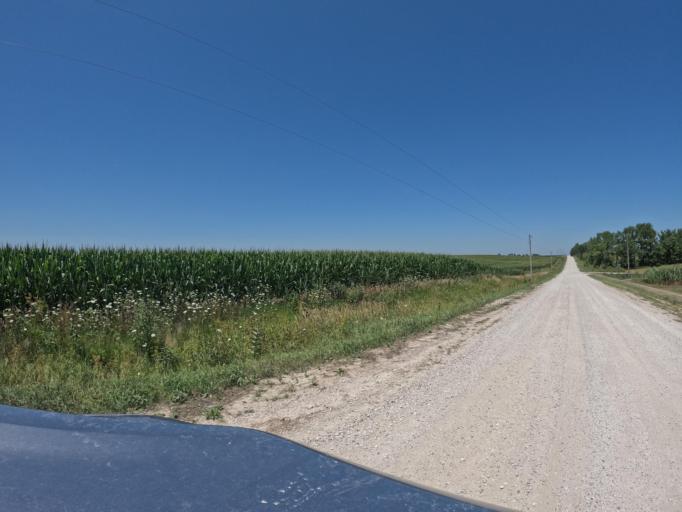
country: US
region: Iowa
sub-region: Keokuk County
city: Sigourney
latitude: 41.4564
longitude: -92.3358
